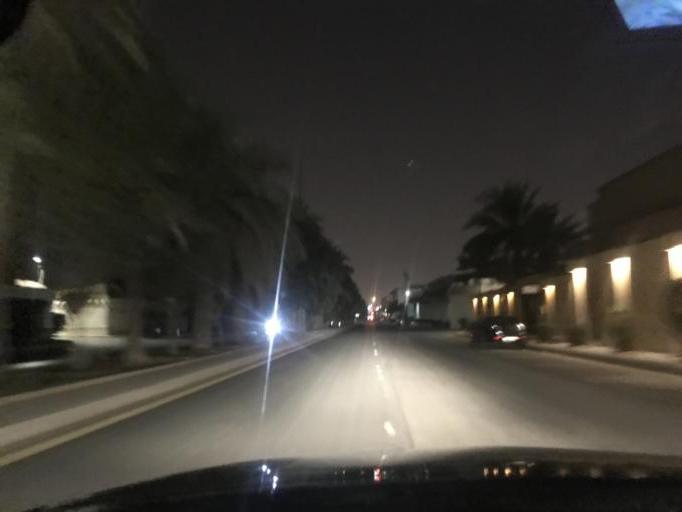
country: SA
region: Ar Riyad
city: Riyadh
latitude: 24.7135
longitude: 46.7777
